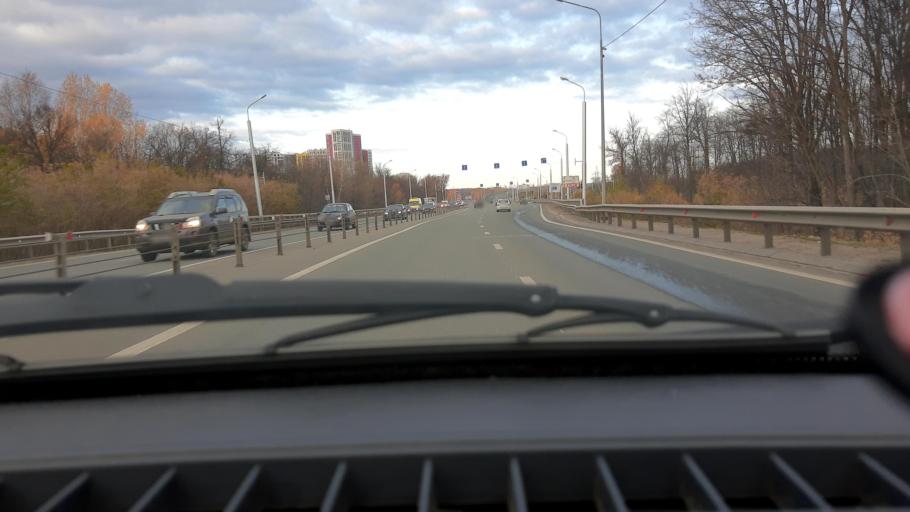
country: RU
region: Bashkortostan
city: Ufa
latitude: 54.6991
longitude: 55.8774
